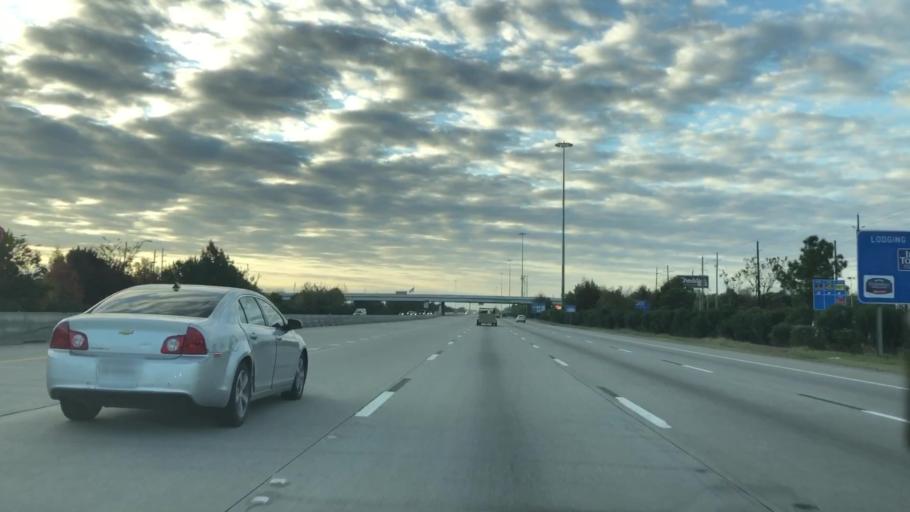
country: US
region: Texas
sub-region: Harris County
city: Spring
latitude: 30.0691
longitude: -95.4351
